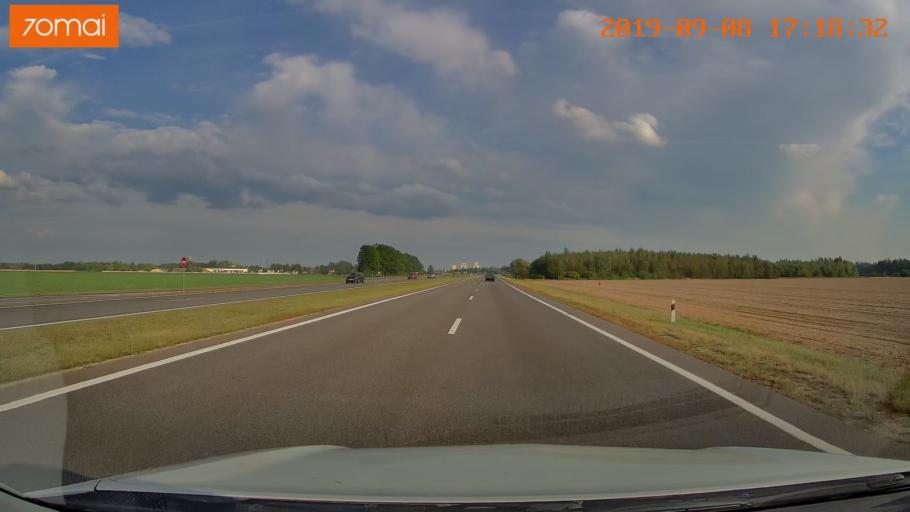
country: BY
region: Grodnenskaya
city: Skidal'
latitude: 53.5865
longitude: 24.1732
